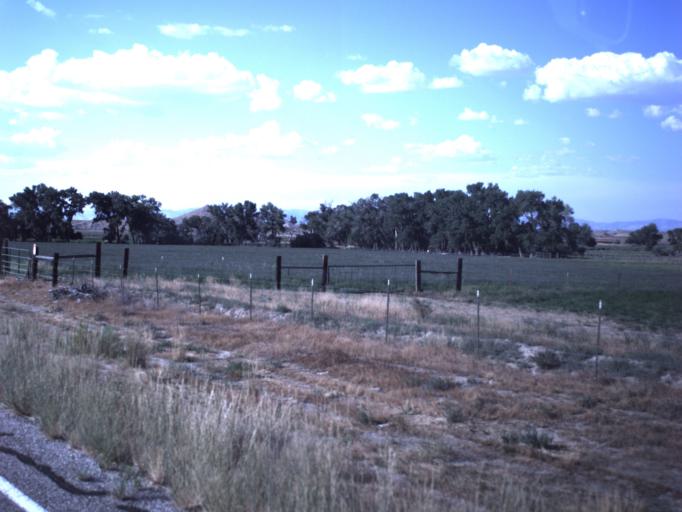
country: US
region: Utah
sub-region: Emery County
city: Huntington
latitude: 39.4225
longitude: -110.8593
